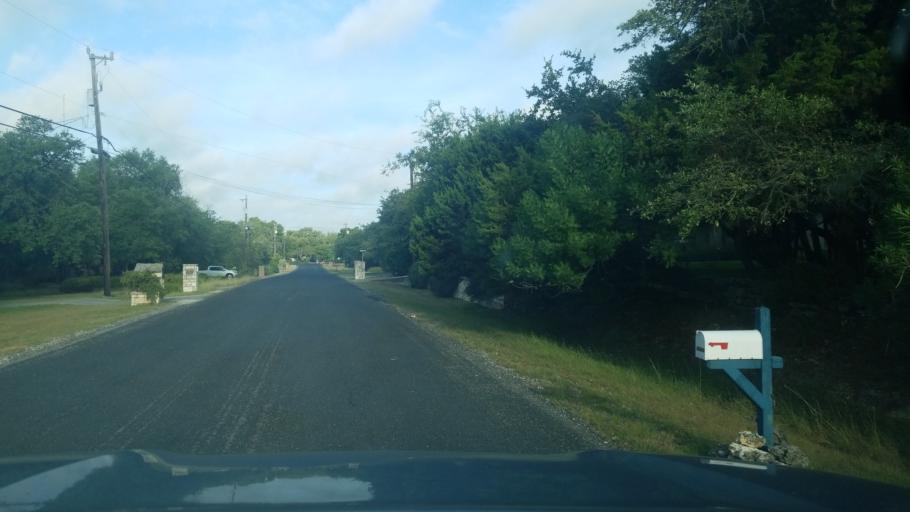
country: US
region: Texas
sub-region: Bexar County
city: Timberwood Park
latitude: 29.6992
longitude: -98.5043
